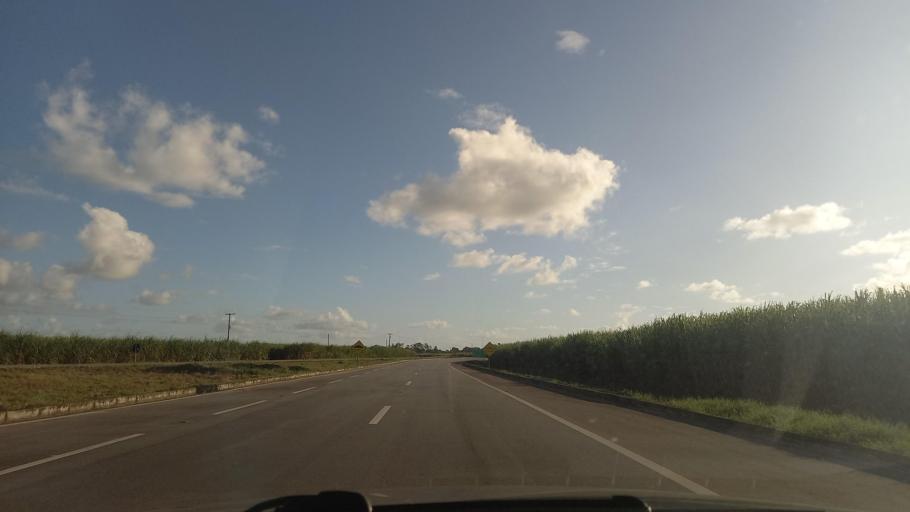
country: BR
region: Alagoas
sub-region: Sao Miguel Dos Campos
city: Sao Miguel dos Campos
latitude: -9.8029
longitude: -36.1985
